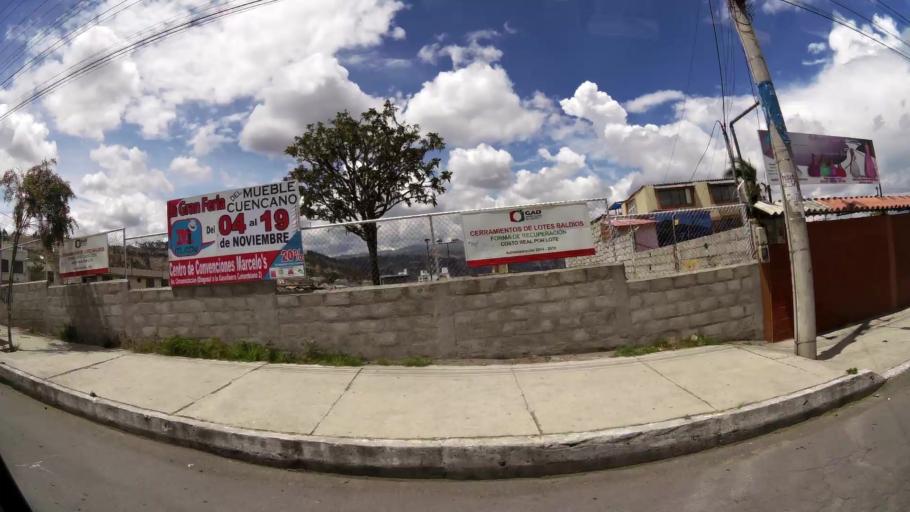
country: EC
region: Tungurahua
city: Ambato
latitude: -1.2793
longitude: -78.6365
